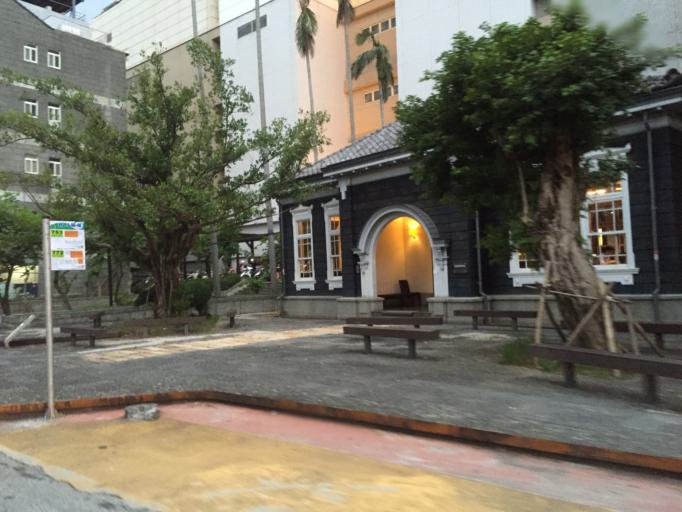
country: TW
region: Taiwan
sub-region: Yilan
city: Yilan
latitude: 24.7539
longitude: 121.7517
